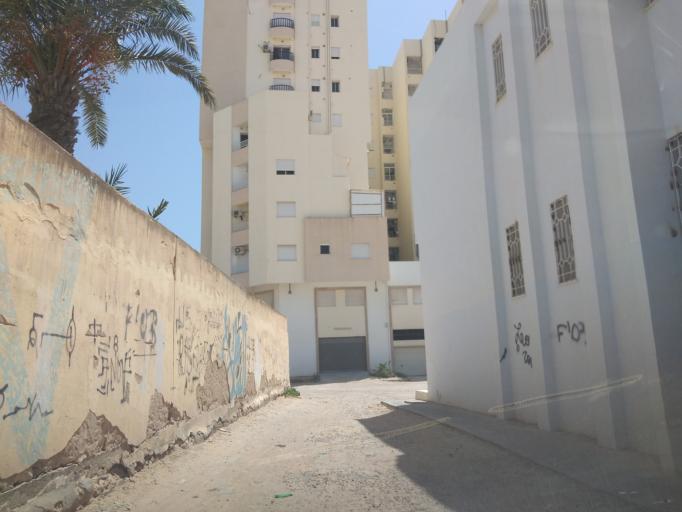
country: TN
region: Safaqis
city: Sfax
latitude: 34.7375
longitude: 10.7513
